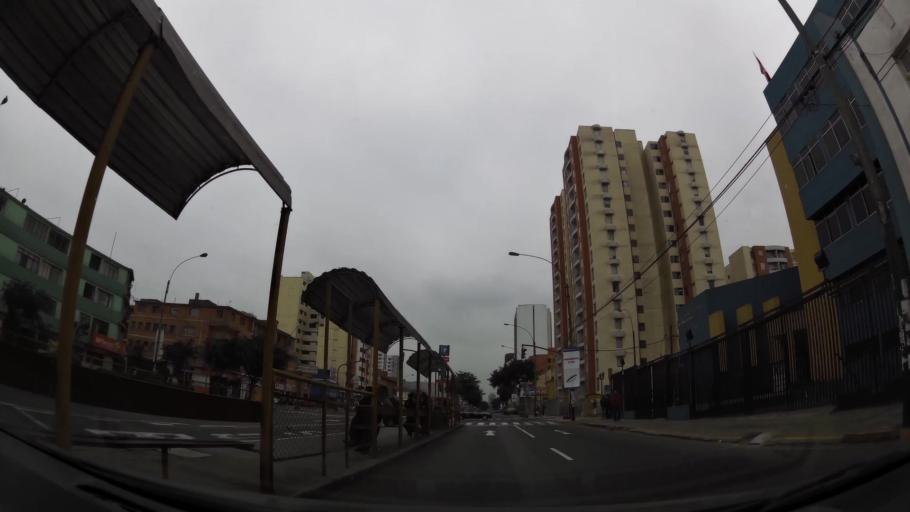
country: PE
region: Lima
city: Lima
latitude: -12.0696
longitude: -77.0491
